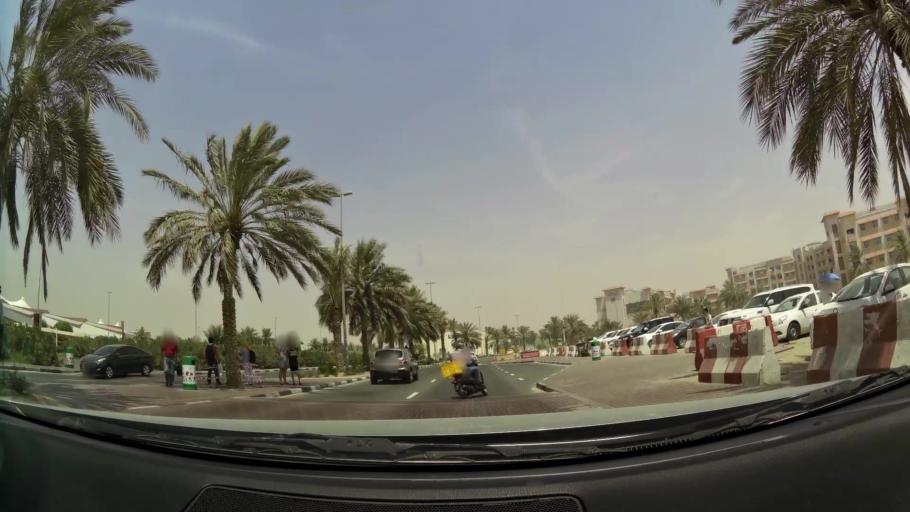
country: AE
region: Ash Shariqah
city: Sharjah
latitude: 25.1730
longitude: 55.4136
